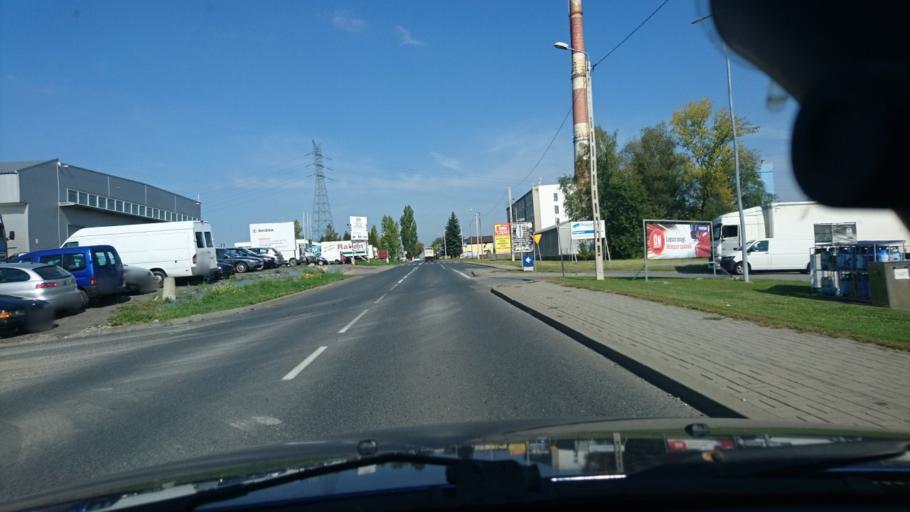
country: PL
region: Silesian Voivodeship
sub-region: Powiat bielski
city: Bestwina
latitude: 49.8695
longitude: 19.0292
